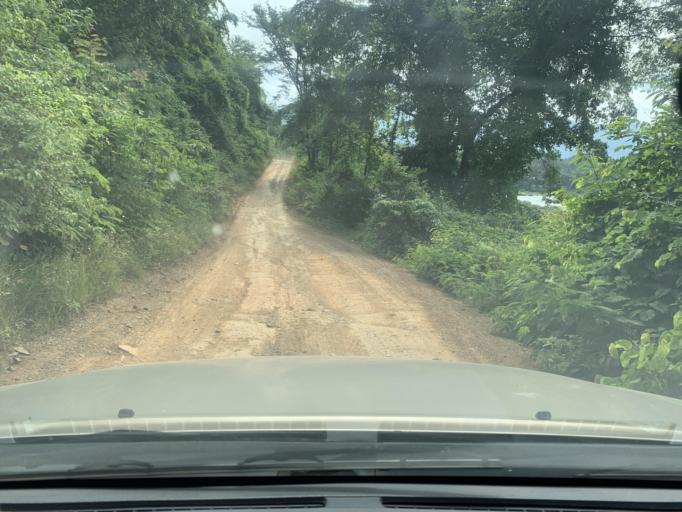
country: LA
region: Louangphabang
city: Louangphabang
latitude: 19.8872
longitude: 102.1932
